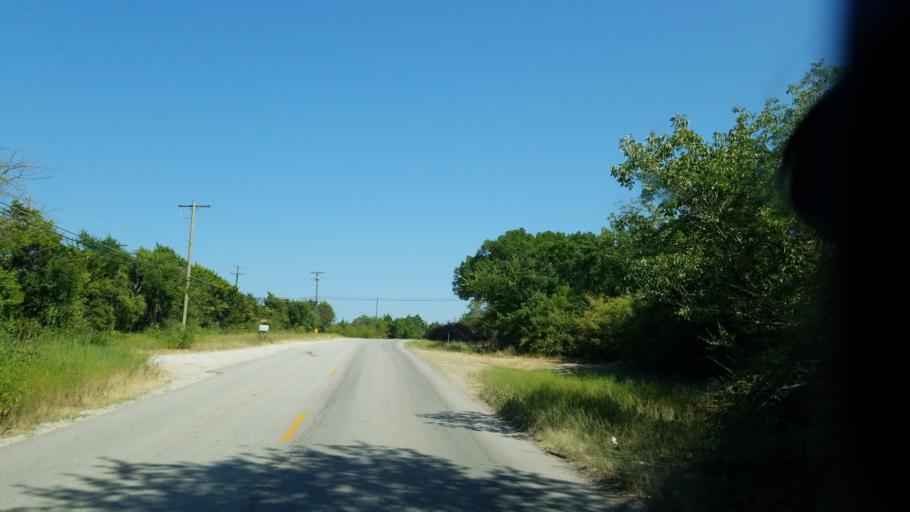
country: US
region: Texas
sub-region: Dallas County
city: Duncanville
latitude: 32.7004
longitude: -96.9252
